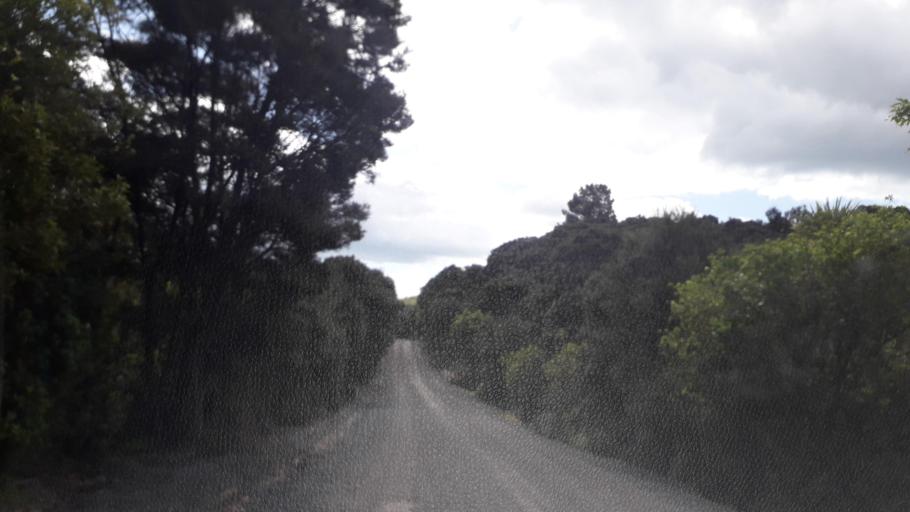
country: NZ
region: Northland
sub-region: Far North District
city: Paihia
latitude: -35.3015
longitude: 174.2208
